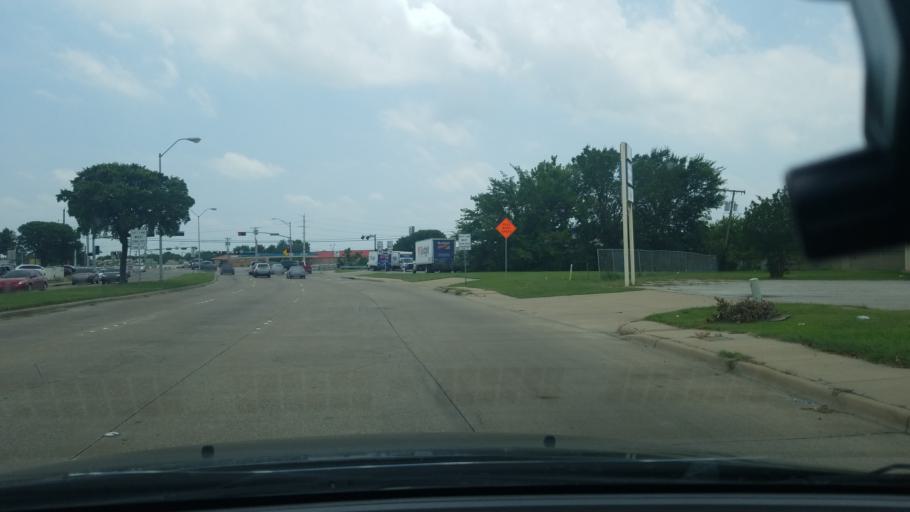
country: US
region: Texas
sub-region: Dallas County
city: Mesquite
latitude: 32.7941
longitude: -96.6121
